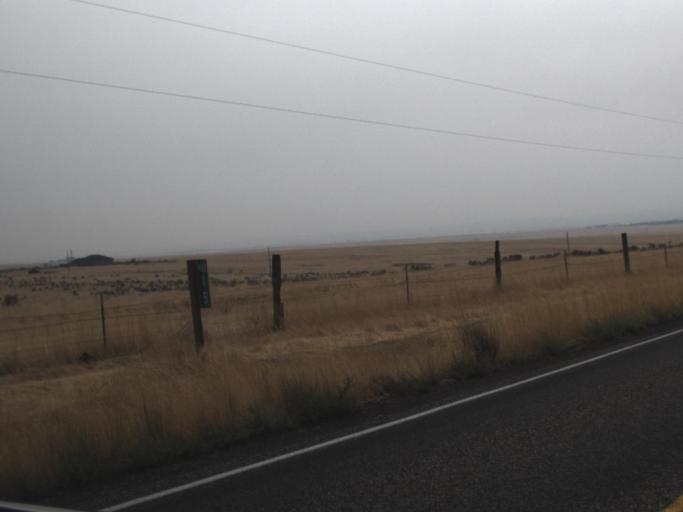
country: US
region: Washington
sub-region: Yakima County
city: Sunnyside
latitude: 46.4079
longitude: -119.9489
